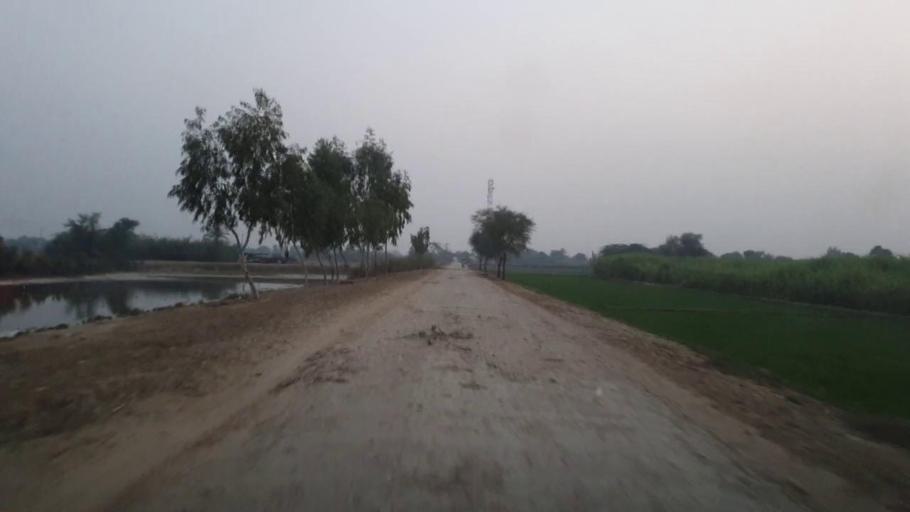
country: PK
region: Sindh
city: Karaundi
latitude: 26.9255
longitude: 68.4299
